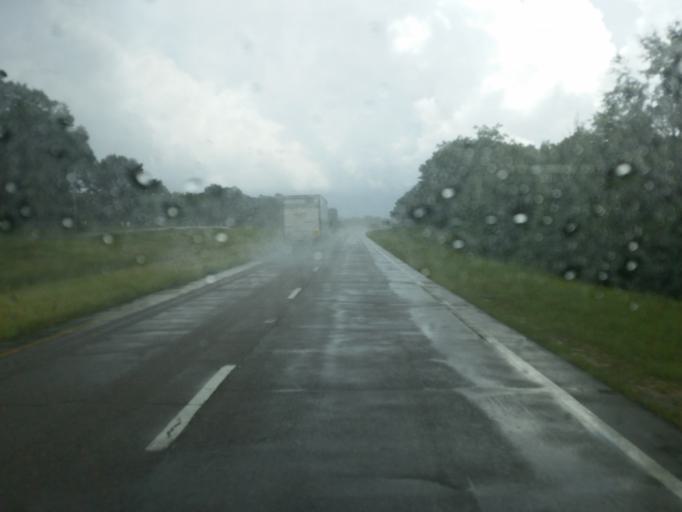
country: US
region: Mississippi
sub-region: George County
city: Lucedale
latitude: 30.9009
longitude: -88.4619
